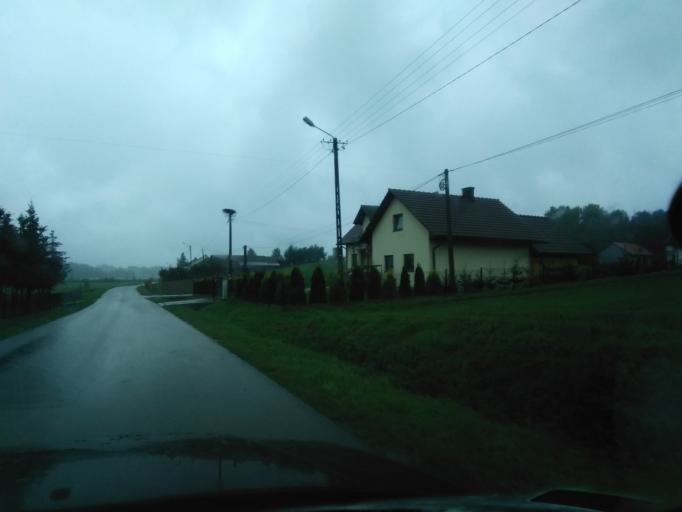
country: PL
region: Subcarpathian Voivodeship
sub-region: Powiat ropczycko-sedziszowski
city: Niedzwiada
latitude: 49.9991
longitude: 21.5525
